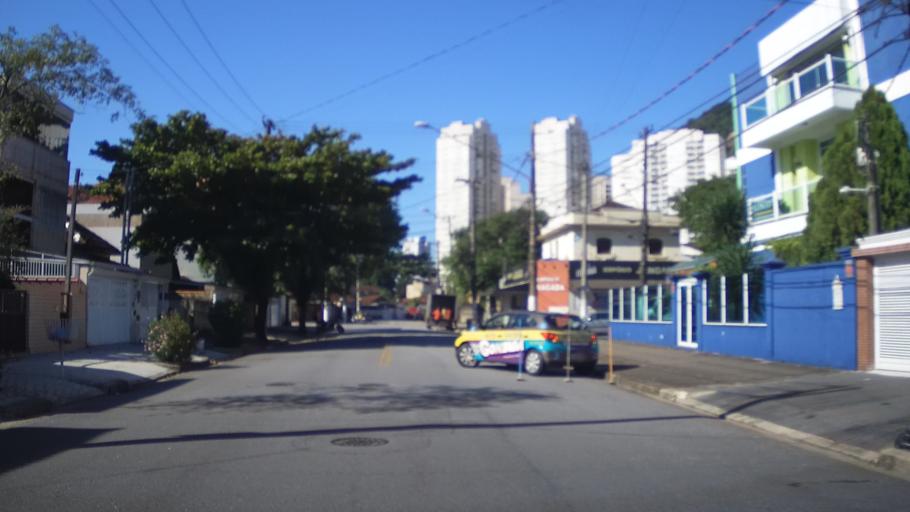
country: BR
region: Sao Paulo
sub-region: Santos
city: Santos
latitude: -23.9552
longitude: -46.3481
